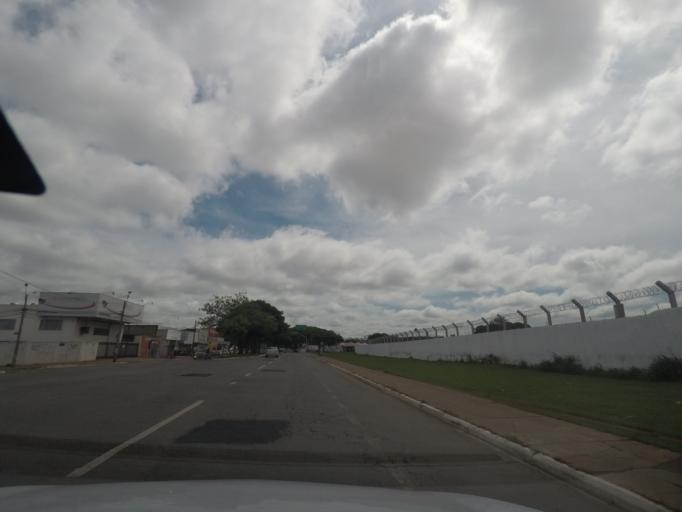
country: BR
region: Goias
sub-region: Goiania
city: Goiania
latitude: -16.6256
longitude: -49.2317
